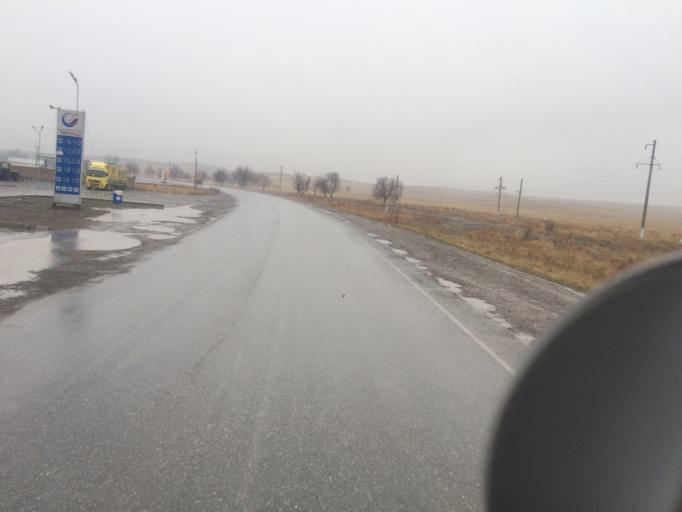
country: KG
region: Chuy
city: Kant
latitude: 43.0040
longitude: 74.8628
